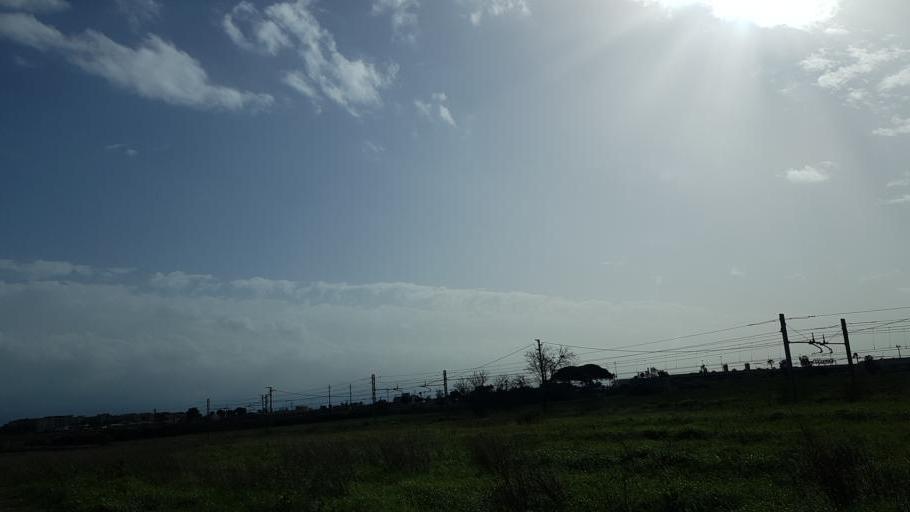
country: IT
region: Apulia
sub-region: Provincia di Brindisi
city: Brindisi
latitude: 40.6238
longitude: 17.8995
